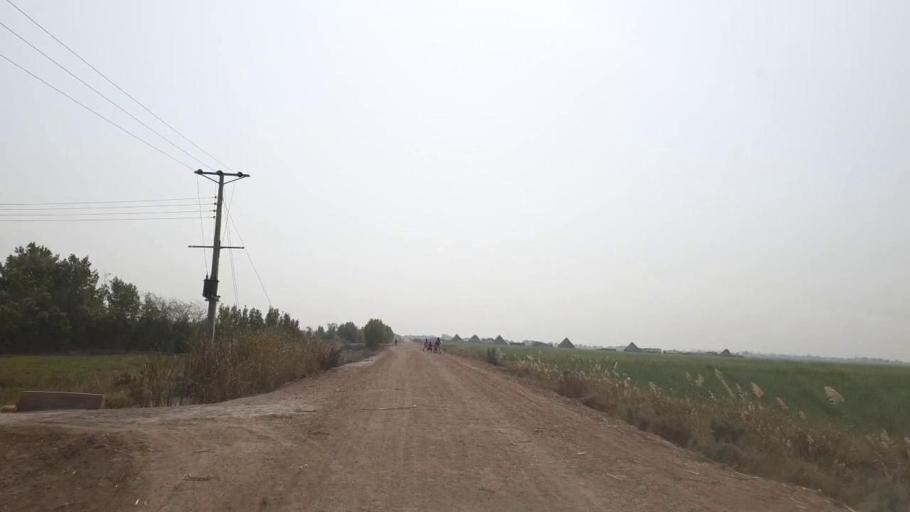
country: PK
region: Sindh
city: Mirpur Khas
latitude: 25.5441
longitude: 69.0603
